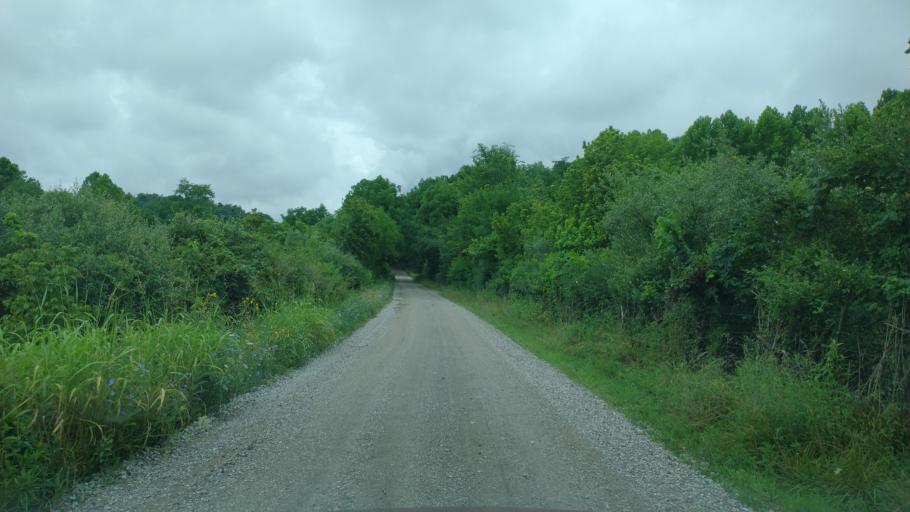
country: US
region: Ohio
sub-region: Meigs County
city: Middleport
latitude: 38.9274
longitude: -82.0589
